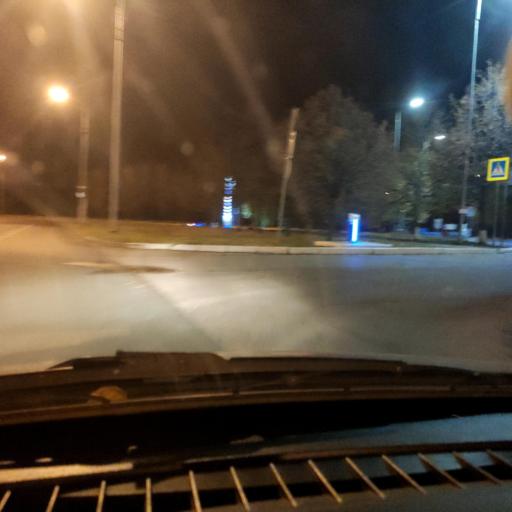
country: RU
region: Samara
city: Tol'yatti
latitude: 53.5010
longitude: 49.2691
